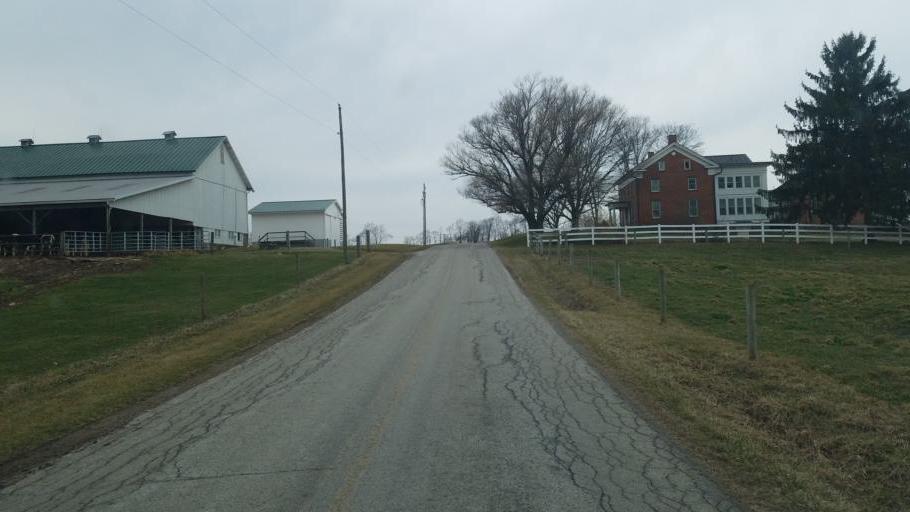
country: US
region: Ohio
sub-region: Richland County
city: Lincoln Heights
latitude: 40.7358
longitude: -82.4211
